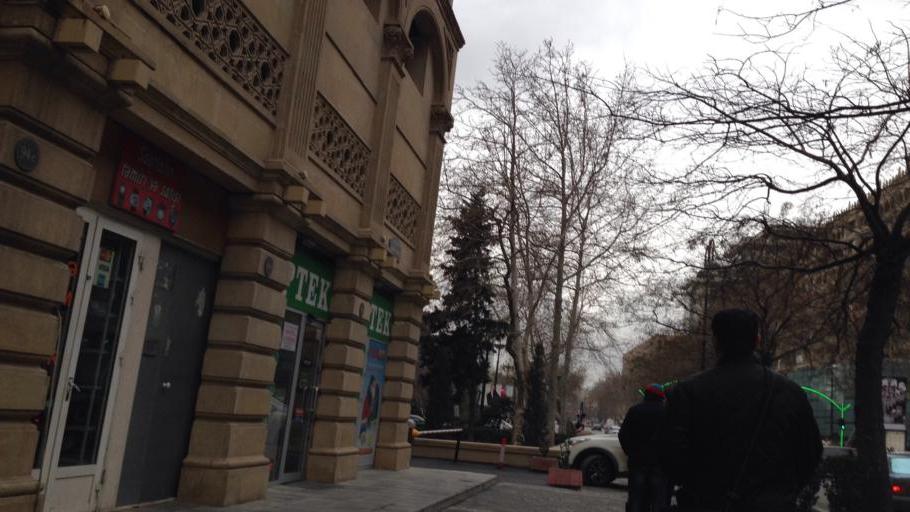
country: AZ
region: Baki
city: Baku
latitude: 40.3762
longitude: 49.8553
